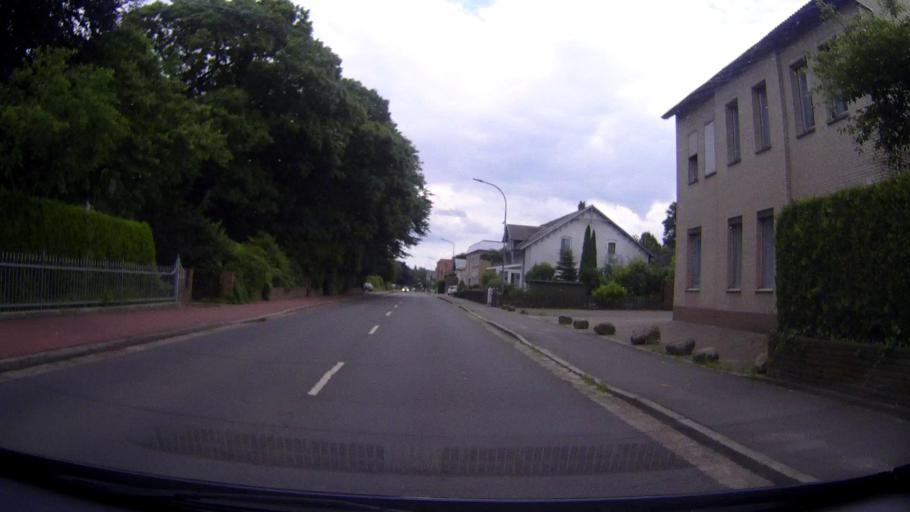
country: DE
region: Schleswig-Holstein
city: Hanerau-Hademarschen
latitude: 54.1254
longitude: 9.4187
